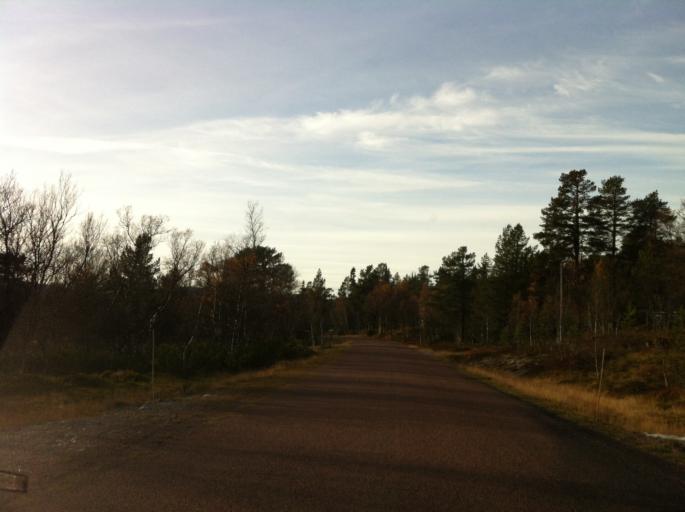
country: NO
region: Hedmark
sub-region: Engerdal
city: Engerdal
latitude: 62.0826
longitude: 12.1279
